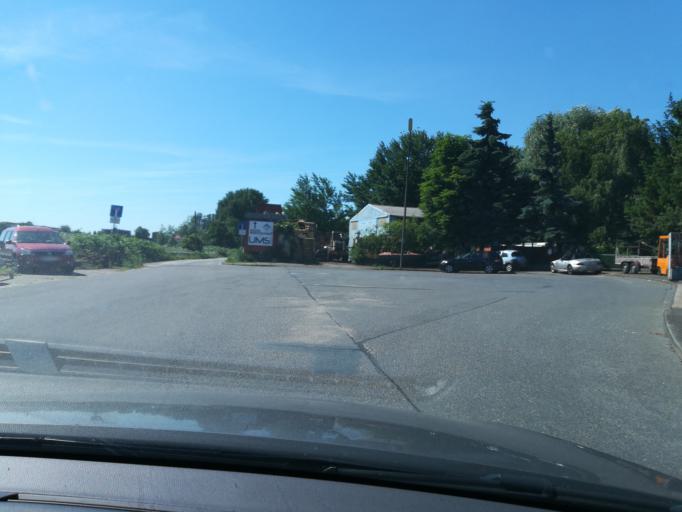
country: DE
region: Hamburg
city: Rothenburgsort
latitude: 53.5256
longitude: 10.0385
